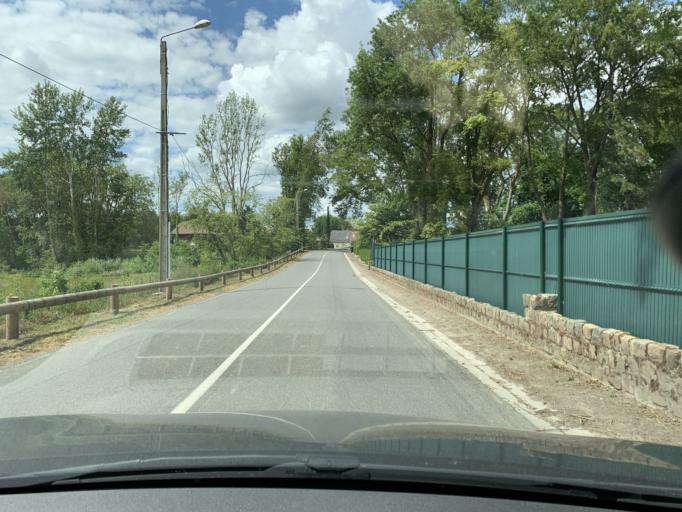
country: FR
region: Nord-Pas-de-Calais
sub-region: Departement du Nord
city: Masnieres
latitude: 50.0764
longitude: 3.2183
